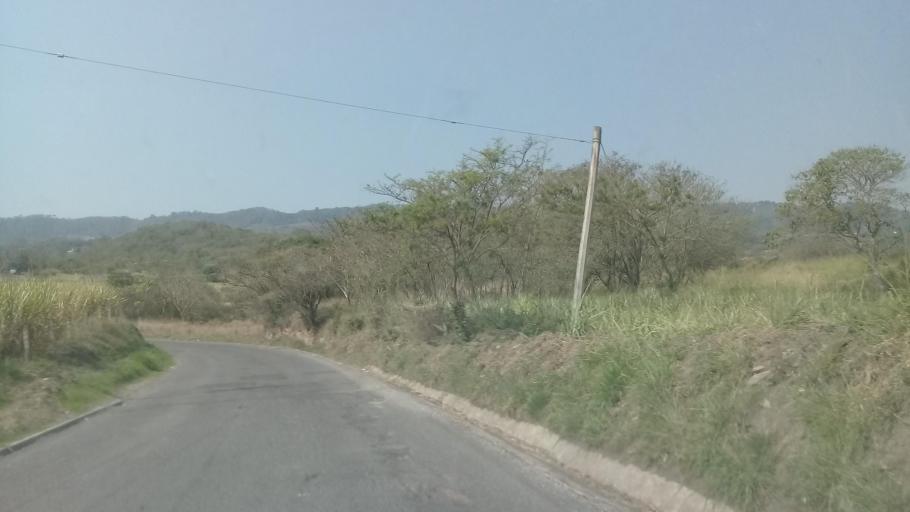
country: MX
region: Veracruz
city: El Castillo
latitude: 19.5811
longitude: -96.8291
